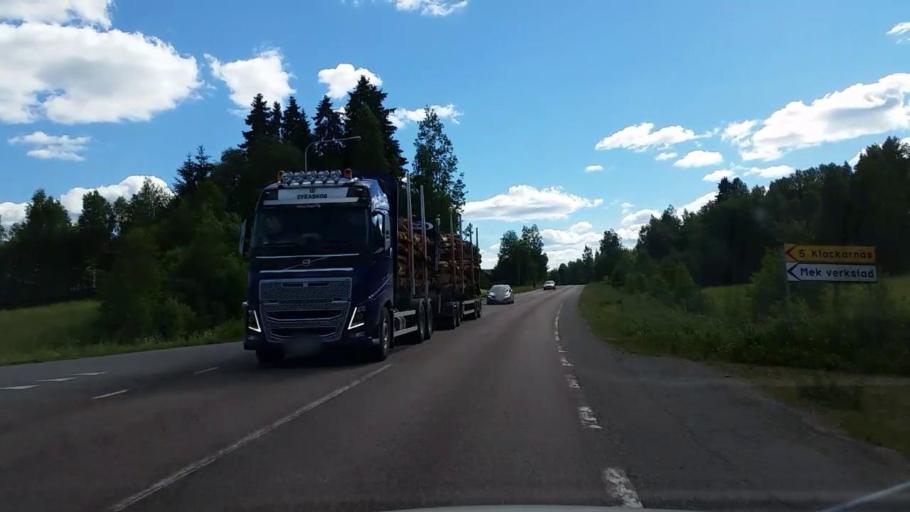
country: SE
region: Dalarna
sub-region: Faluns Kommun
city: Svardsjo
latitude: 60.8411
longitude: 15.7620
